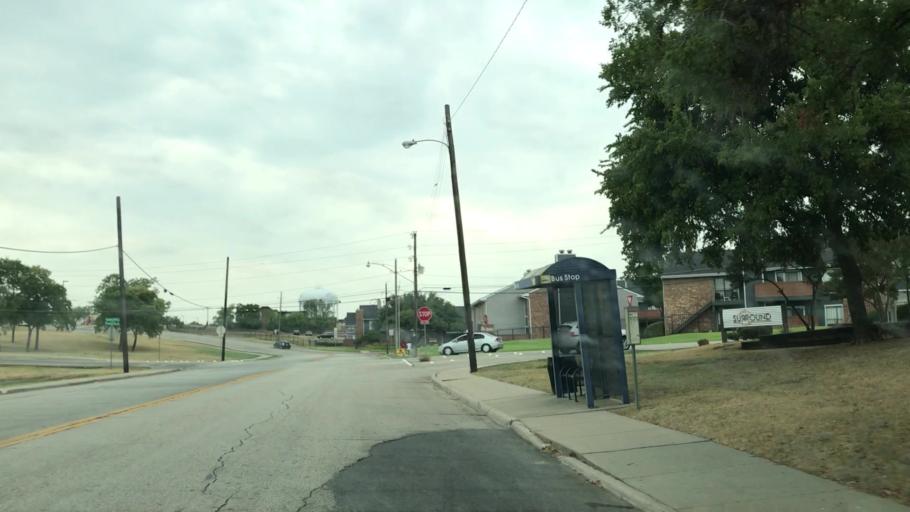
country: US
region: Texas
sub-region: Dallas County
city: Irving
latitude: 32.8608
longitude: -96.9886
